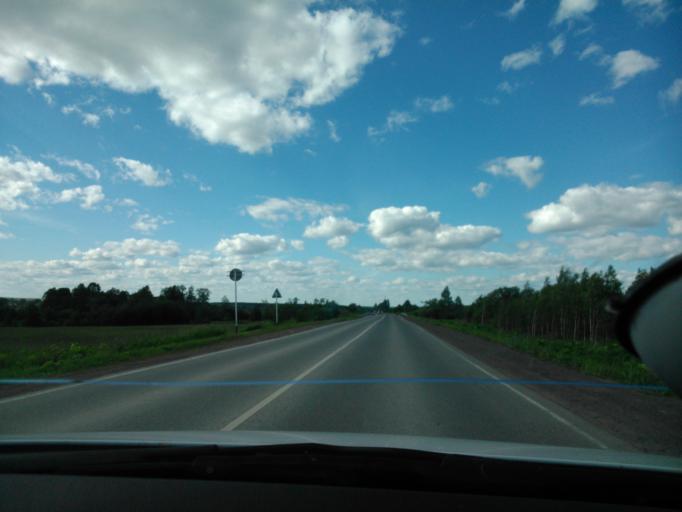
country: RU
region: Perm
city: Ust'-Kachka
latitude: 57.9298
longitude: 55.7615
